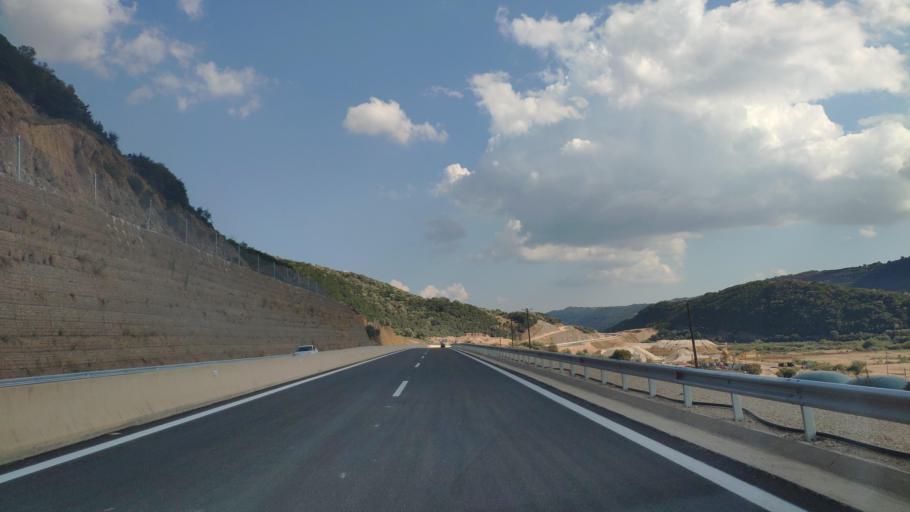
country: GR
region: West Greece
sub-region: Nomos Aitolias kai Akarnanias
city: Katouna
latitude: 38.7957
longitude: 21.1383
